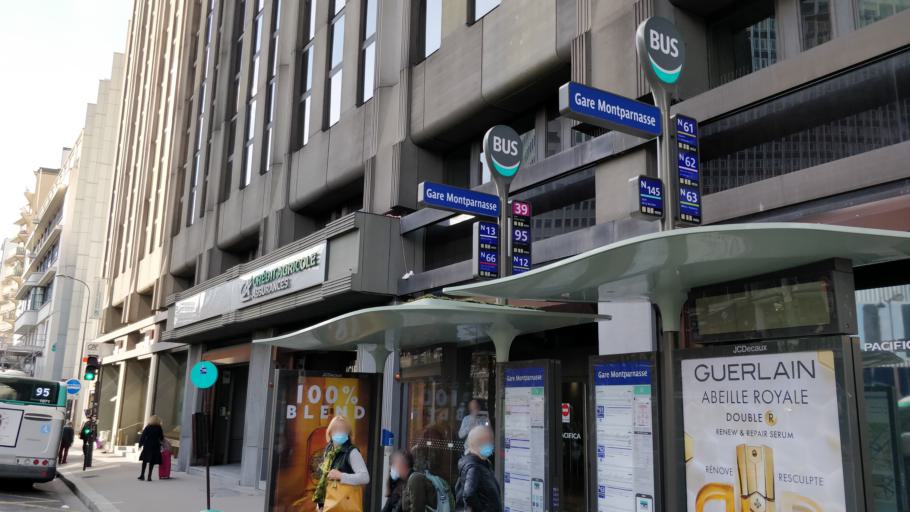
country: FR
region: Ile-de-France
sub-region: Departement des Hauts-de-Seine
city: Montrouge
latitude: 48.8421
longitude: 2.3202
